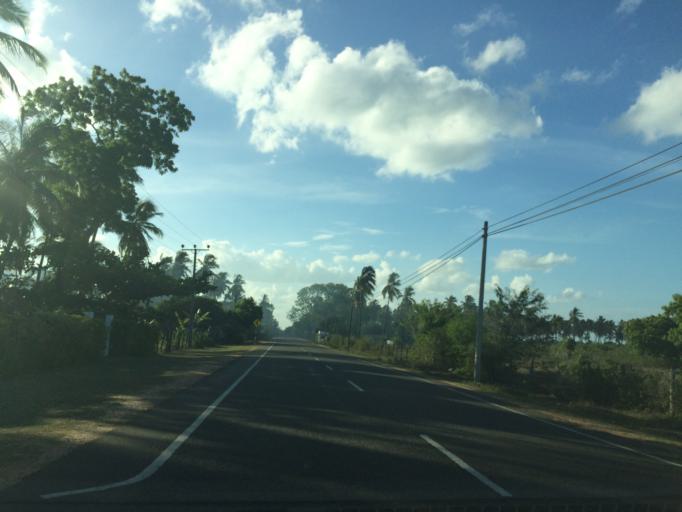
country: LK
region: Eastern Province
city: Trincomalee
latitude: 8.7109
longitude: 81.1774
